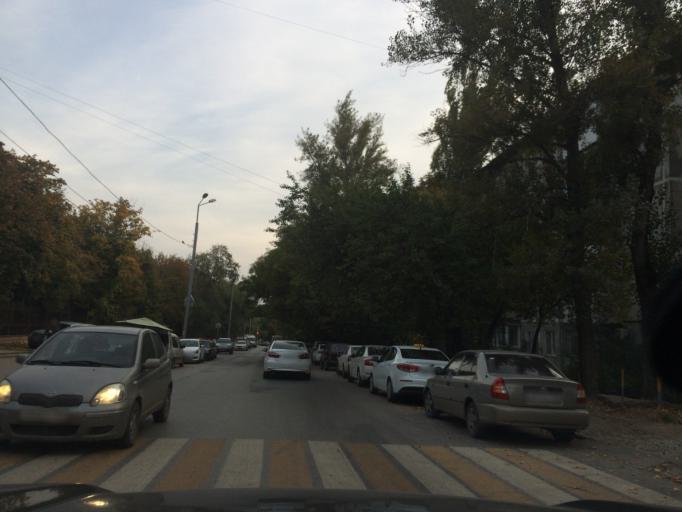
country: RU
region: Rostov
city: Rostov-na-Donu
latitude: 47.2051
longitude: 39.6215
